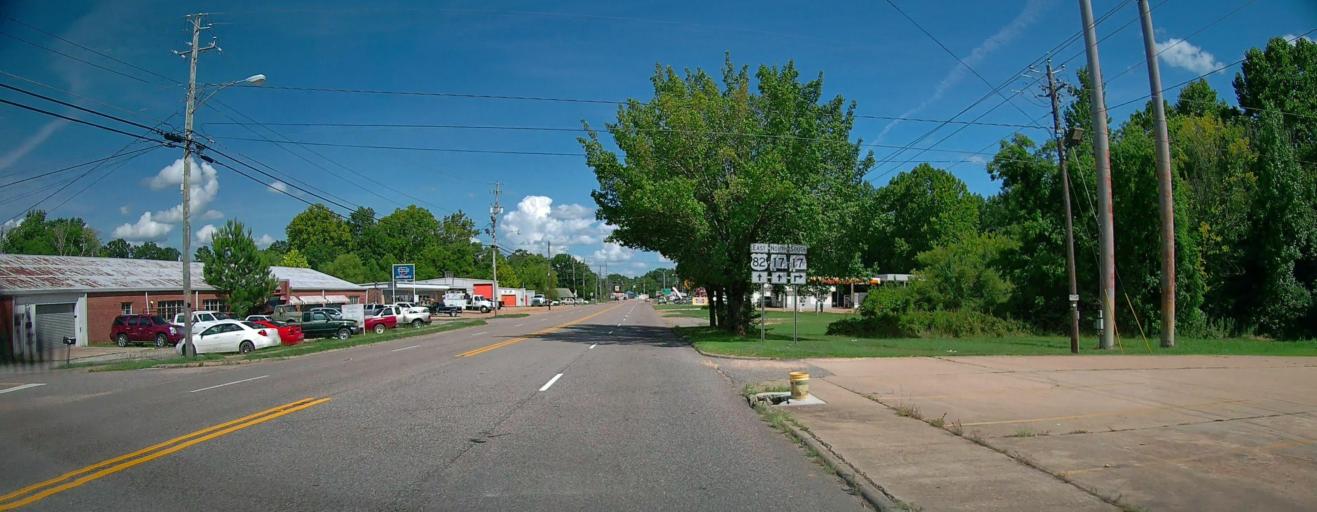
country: US
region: Alabama
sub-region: Pickens County
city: Reform
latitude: 33.3810
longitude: -88.0204
